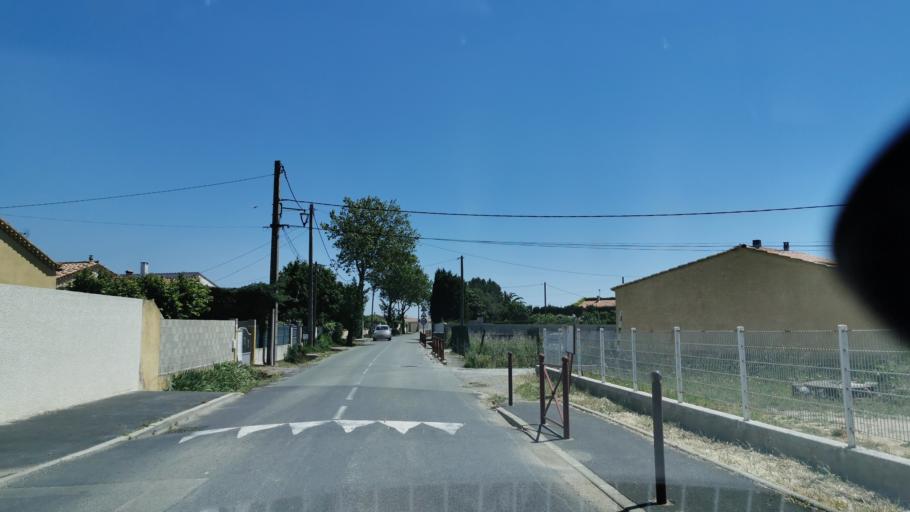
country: FR
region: Languedoc-Roussillon
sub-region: Departement de l'Aude
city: Marcorignan
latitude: 43.2447
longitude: 2.9023
